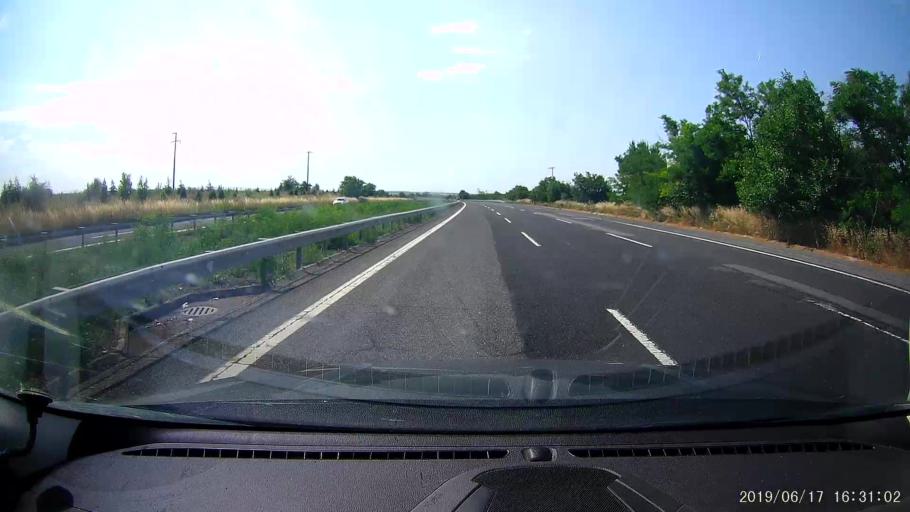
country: TR
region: Tekirdag
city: Beyazkoy
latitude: 41.3573
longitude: 27.6399
